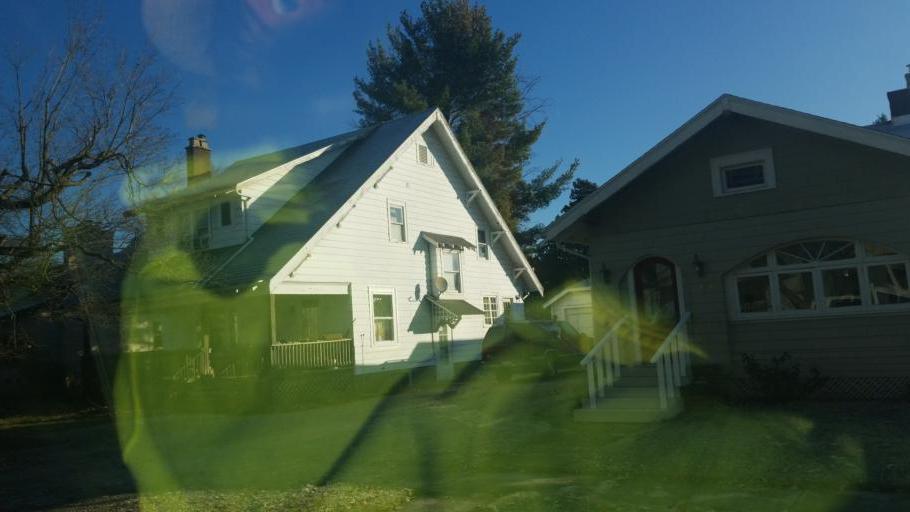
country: US
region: Ohio
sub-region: Marion County
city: Marion
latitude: 40.5818
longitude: -83.1148
